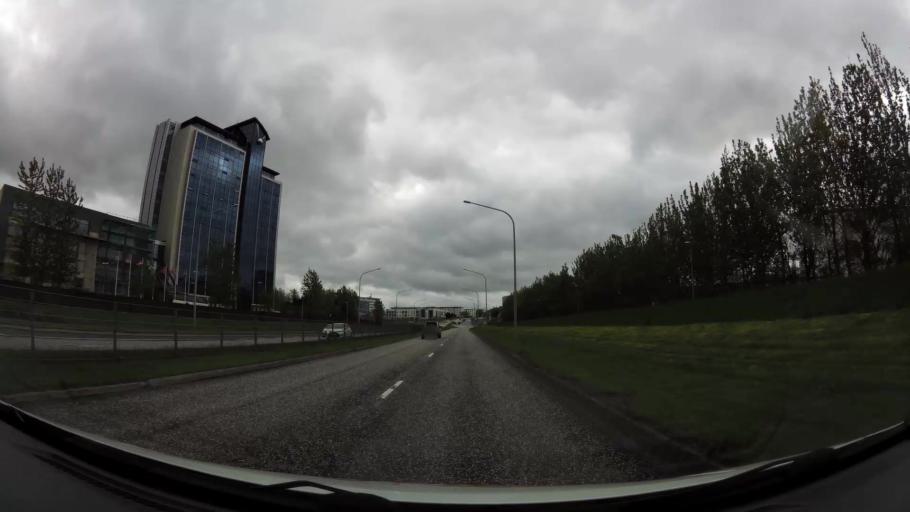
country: IS
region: Capital Region
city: Reykjavik
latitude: 64.1429
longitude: -21.8928
